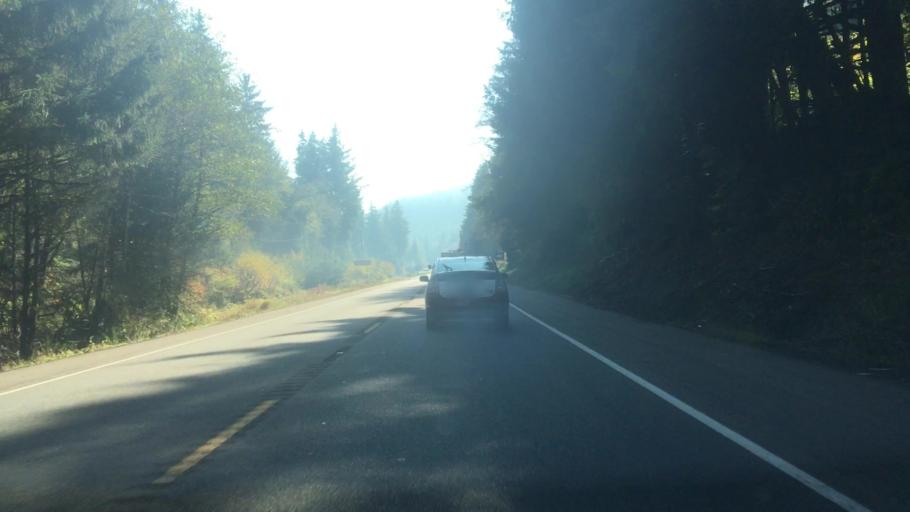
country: US
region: Washington
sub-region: Grays Harbor County
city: Central Park
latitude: 46.9236
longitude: -123.7173
